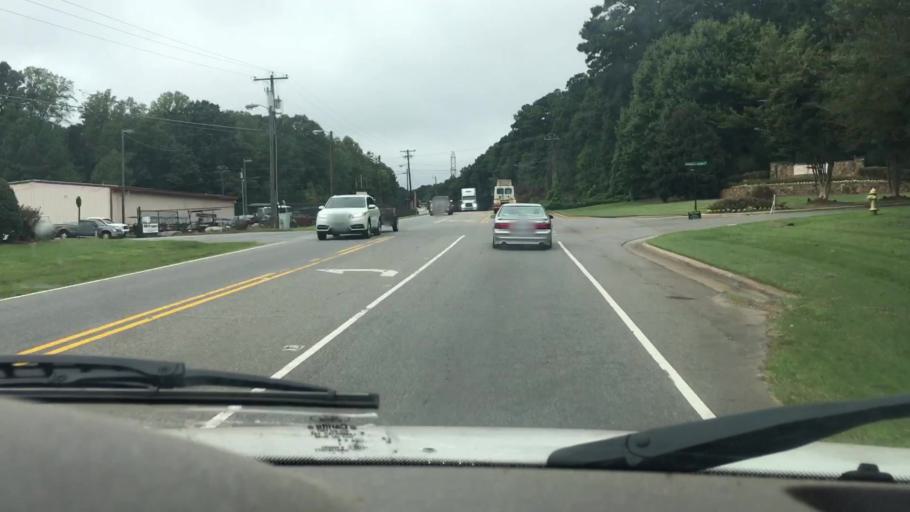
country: US
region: North Carolina
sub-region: Catawba County
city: Lake Norman of Catawba
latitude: 35.6051
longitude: -80.9300
